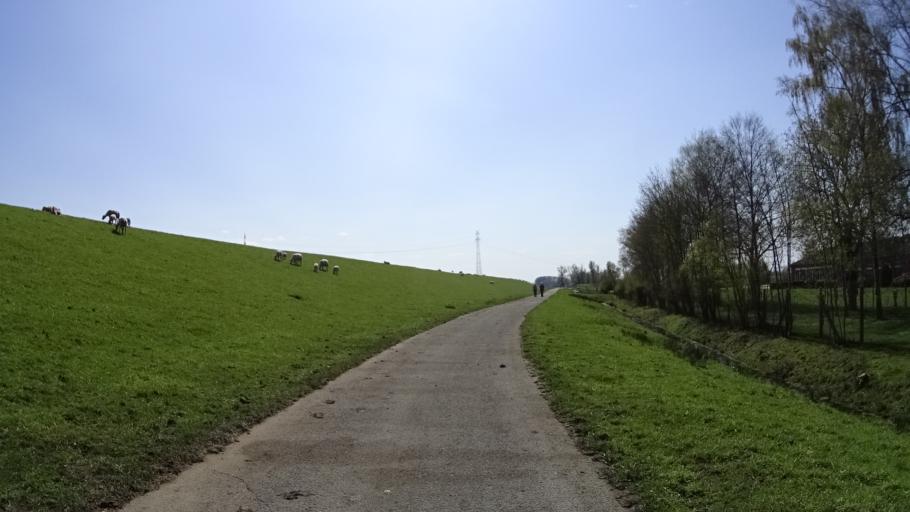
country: DE
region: Lower Saxony
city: Weener
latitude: 53.1571
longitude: 7.3723
